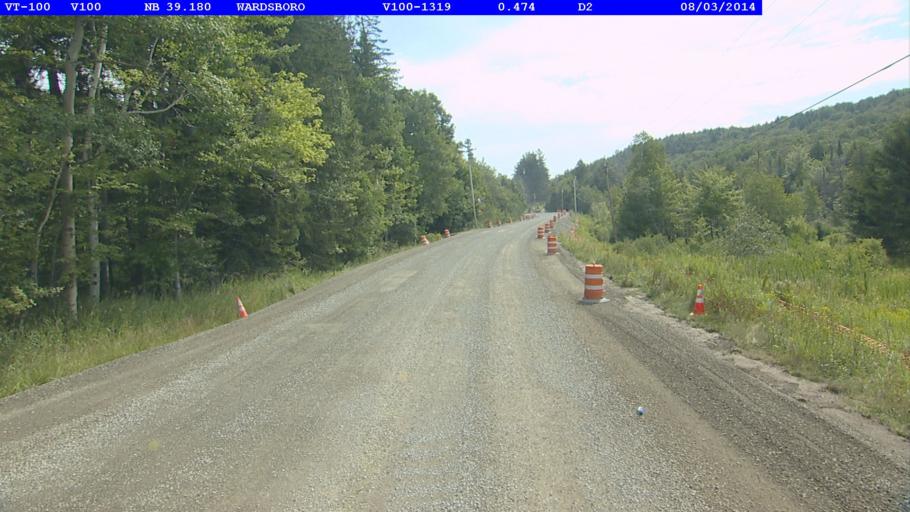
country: US
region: Vermont
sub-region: Windham County
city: Dover
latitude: 43.0107
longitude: -72.8697
